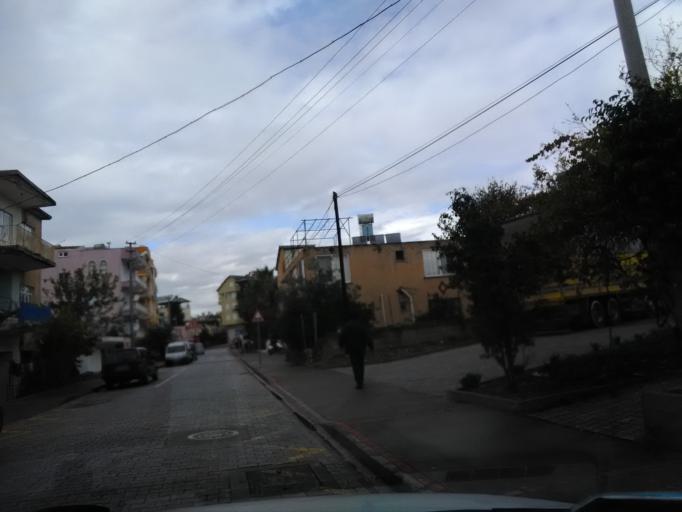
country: TR
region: Antalya
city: Gazipasa
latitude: 36.2716
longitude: 32.3146
